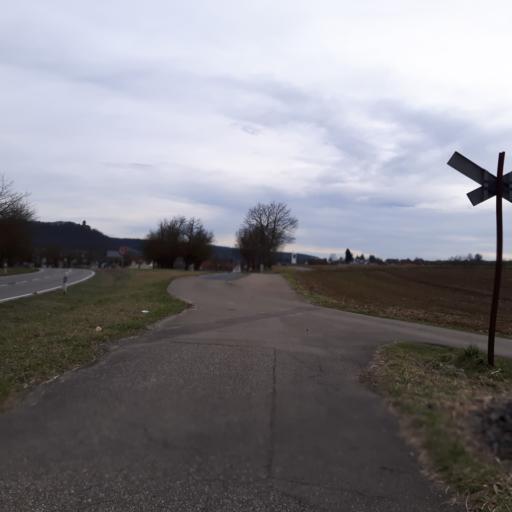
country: DE
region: Baden-Wuerttemberg
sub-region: Regierungsbezirk Stuttgart
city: Beilstein
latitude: 49.0336
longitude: 9.3164
